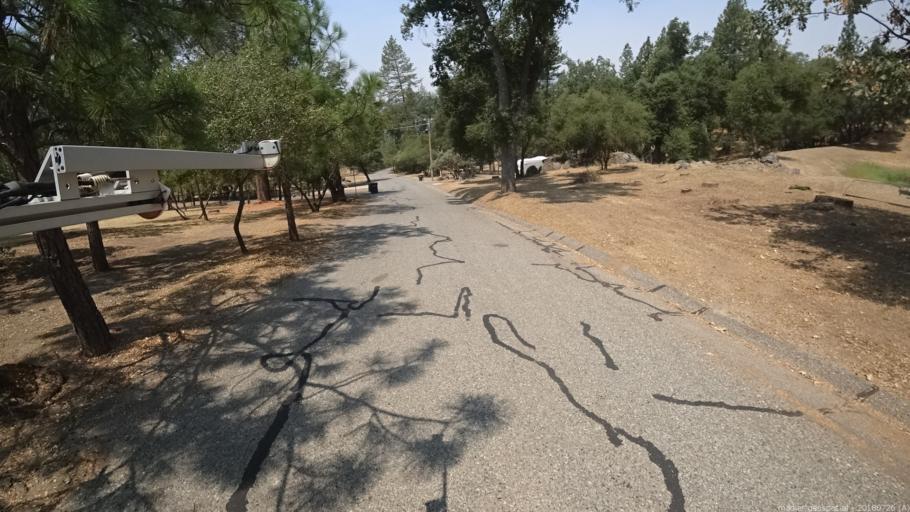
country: US
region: California
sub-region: Madera County
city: Oakhurst
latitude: 37.2847
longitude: -119.6436
